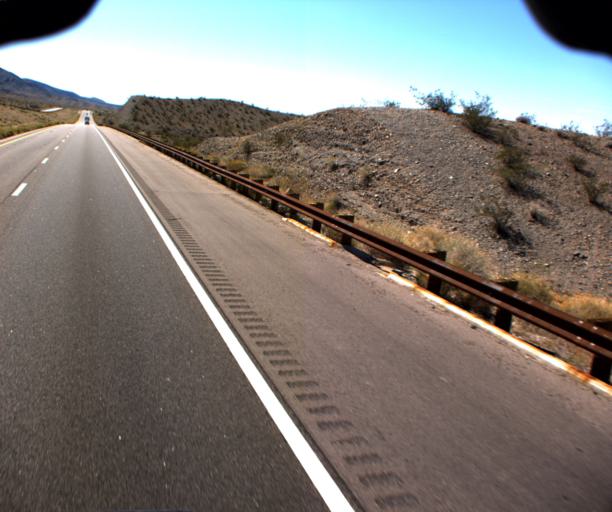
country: US
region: Nevada
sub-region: Clark County
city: Boulder City
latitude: 35.9423
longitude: -114.6427
